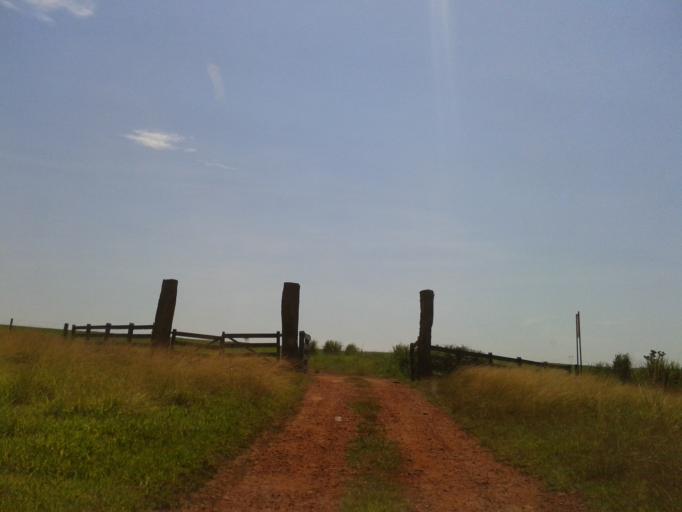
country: BR
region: Minas Gerais
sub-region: Santa Vitoria
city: Santa Vitoria
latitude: -19.0716
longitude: -50.4804
